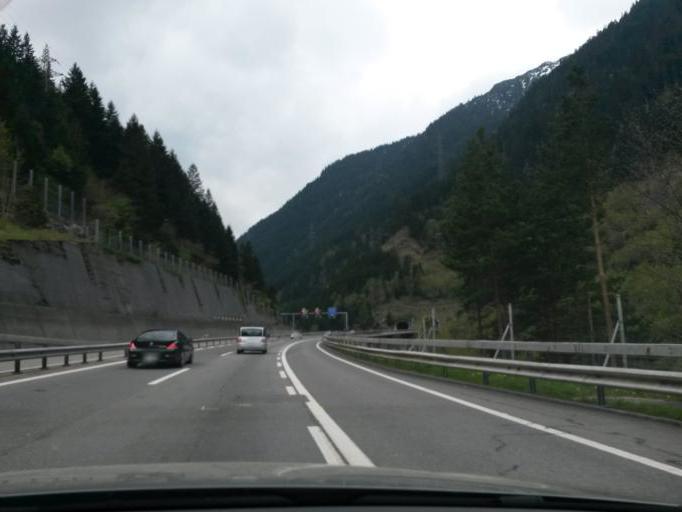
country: CH
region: Uri
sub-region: Uri
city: Andermatt
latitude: 46.6893
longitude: 8.5948
